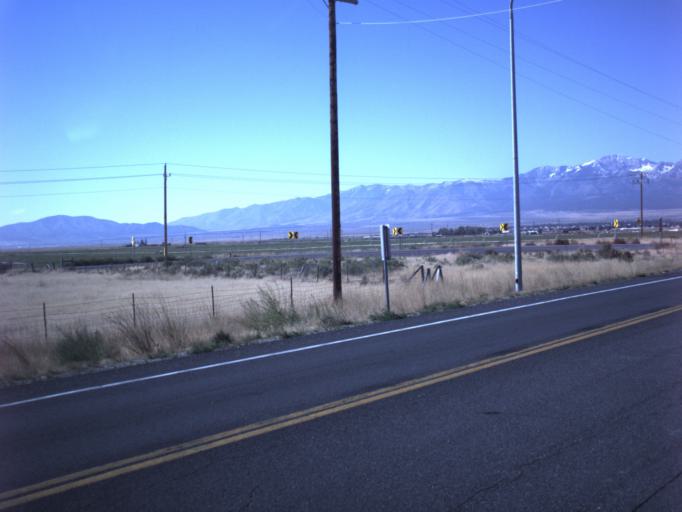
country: US
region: Utah
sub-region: Tooele County
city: Grantsville
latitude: 40.6017
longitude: -112.4038
